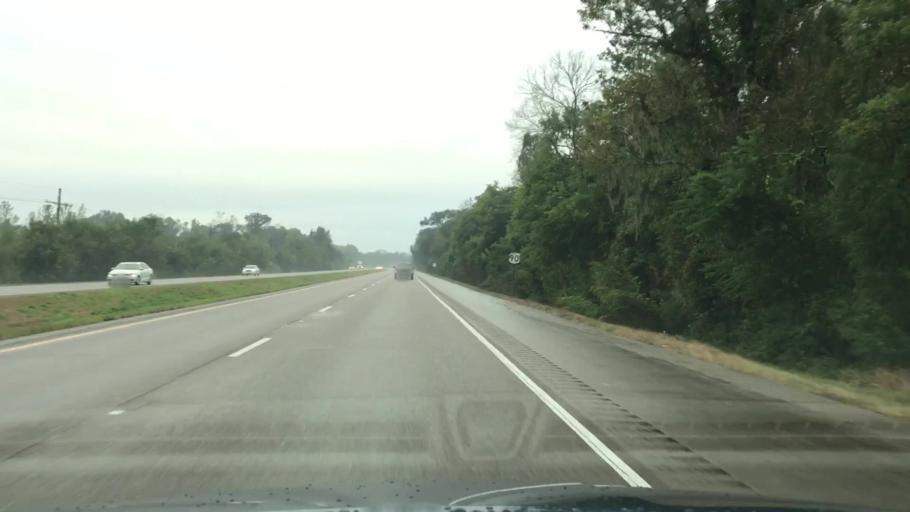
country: US
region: Louisiana
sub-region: Saint Charles Parish
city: Paradis
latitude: 29.8519
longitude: -90.4480
